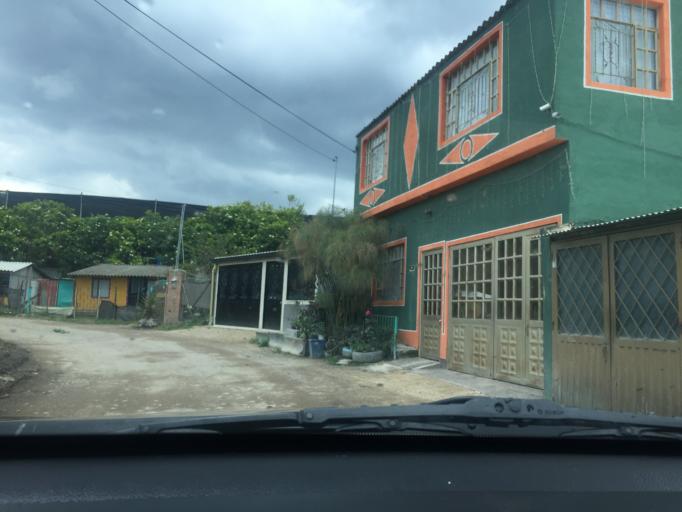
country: CO
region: Cundinamarca
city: Facatativa
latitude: 4.8025
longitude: -74.3030
